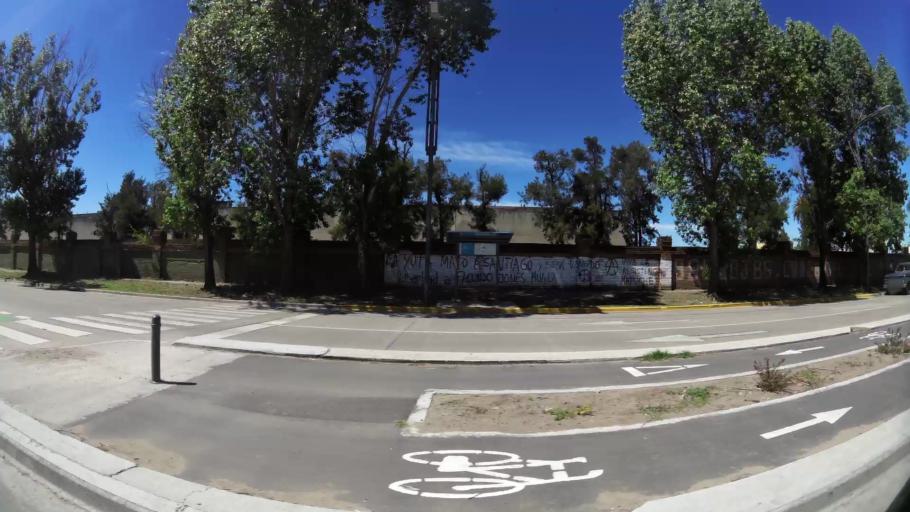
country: AR
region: Santa Fe
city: Perez
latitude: -32.9592
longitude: -60.7110
